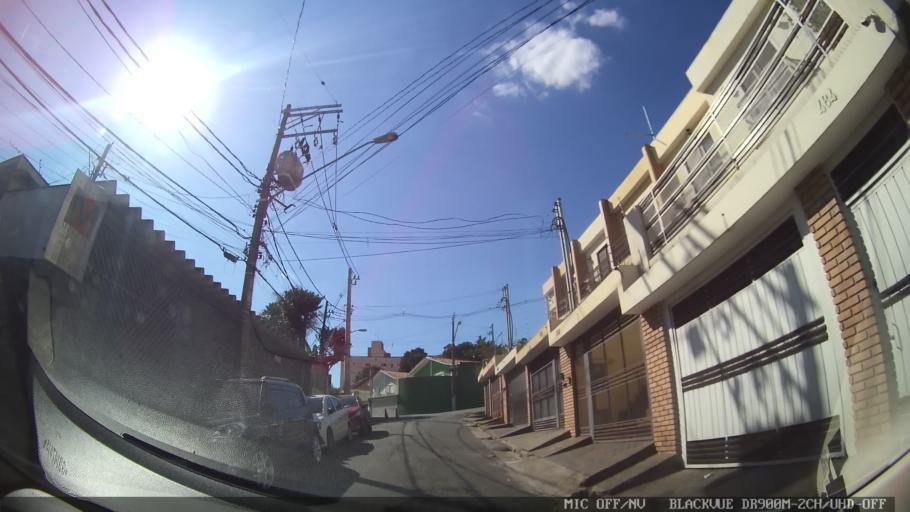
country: BR
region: Sao Paulo
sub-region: Sao Paulo
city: Sao Paulo
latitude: -23.4898
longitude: -46.6460
